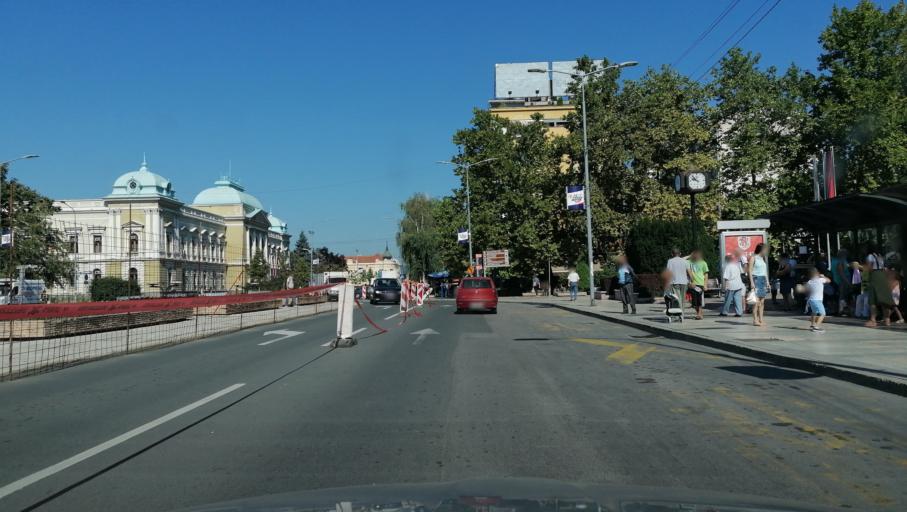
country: RS
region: Central Serbia
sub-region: Rasinski Okrug
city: Krusevac
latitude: 43.5829
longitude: 21.3265
